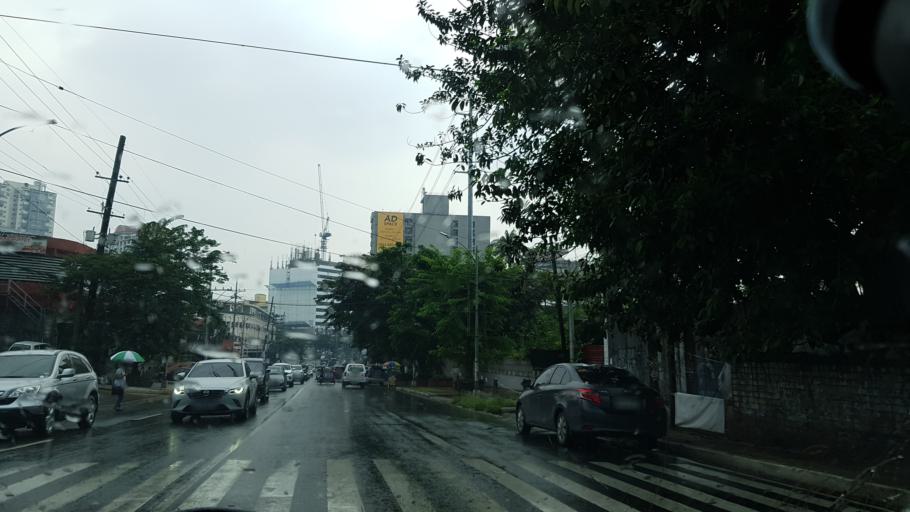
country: PH
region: Calabarzon
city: Del Monte
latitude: 14.6403
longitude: 121.0265
